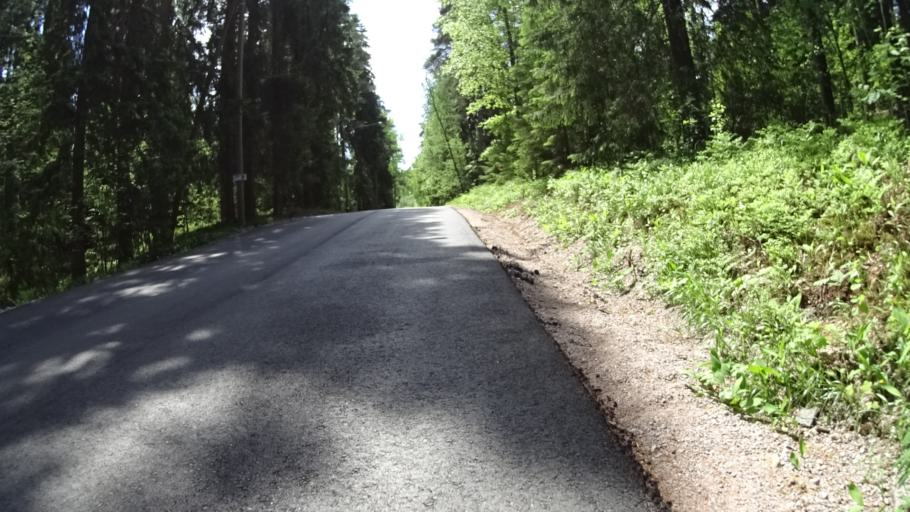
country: FI
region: Uusimaa
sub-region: Helsinki
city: Espoo
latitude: 60.2569
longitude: 24.6529
